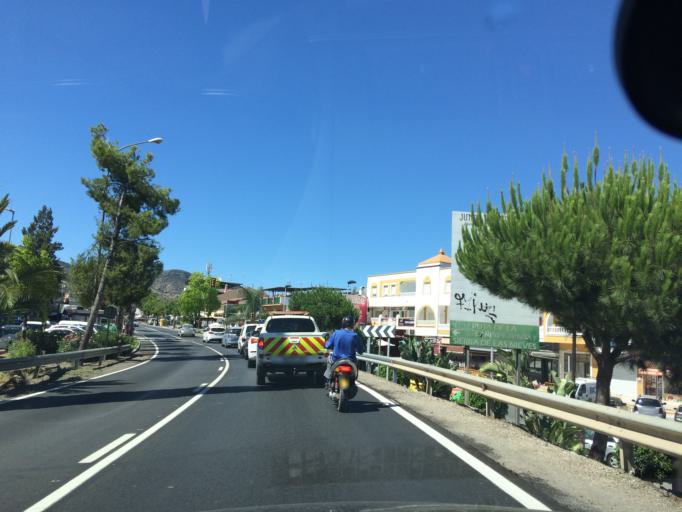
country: ES
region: Andalusia
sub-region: Provincia de Malaga
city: Estacion de Cartama
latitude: 36.7349
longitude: -4.6122
